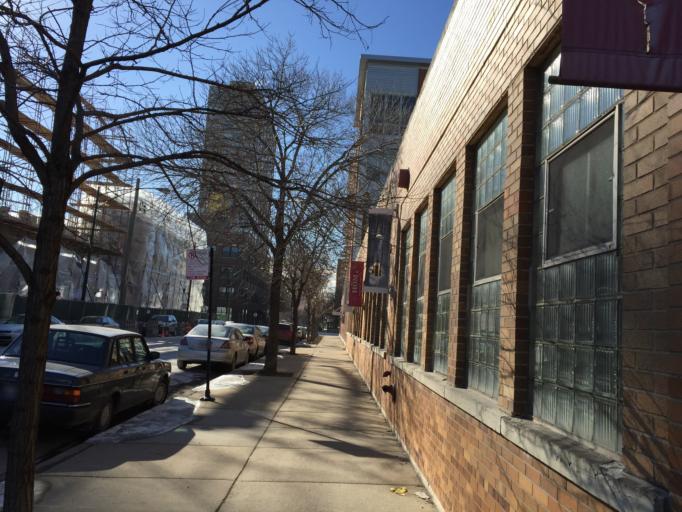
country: US
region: Illinois
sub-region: Cook County
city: Chicago
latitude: 41.8544
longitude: -87.6210
